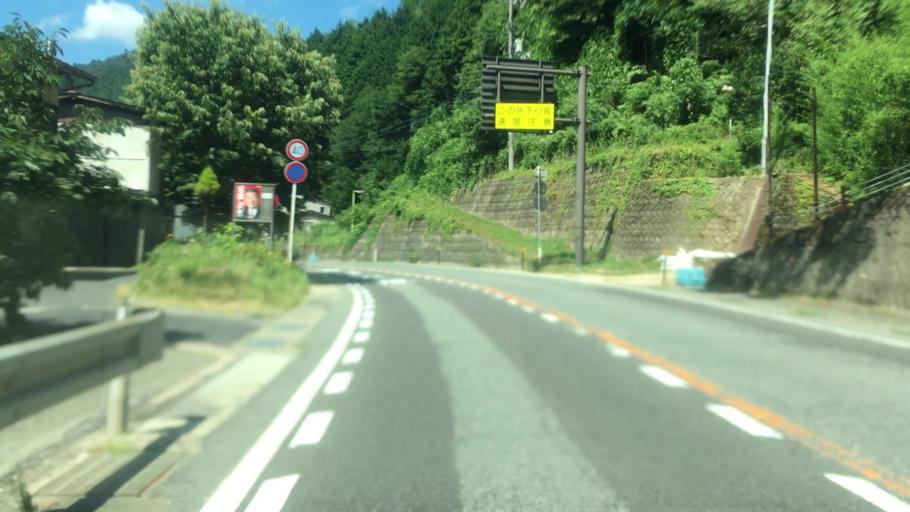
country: JP
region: Tottori
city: Tottori
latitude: 35.2642
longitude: 134.2287
